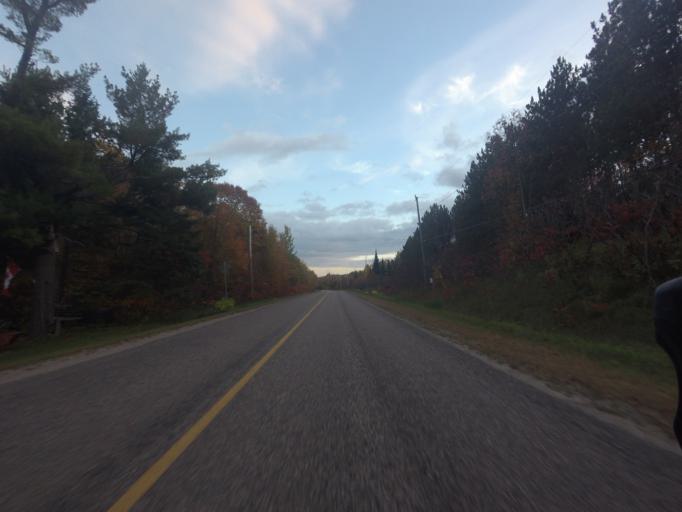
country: CA
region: Ontario
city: Renfrew
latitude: 45.3943
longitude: -76.9503
